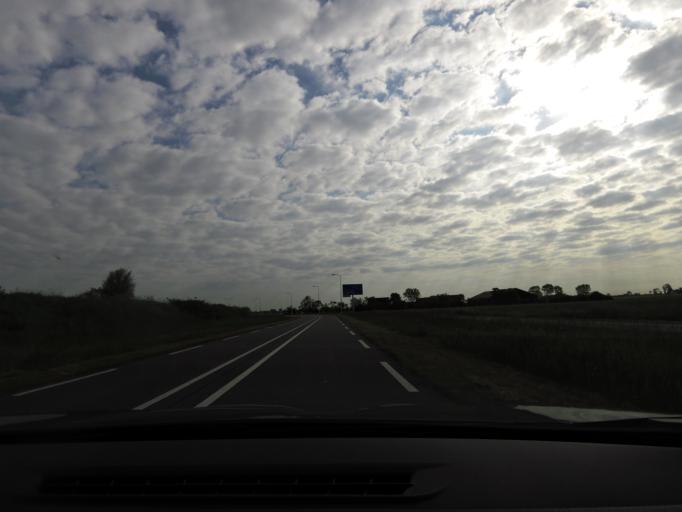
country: NL
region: Zeeland
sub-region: Schouwen-Duiveland
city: Renesse
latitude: 51.7237
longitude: 3.7787
